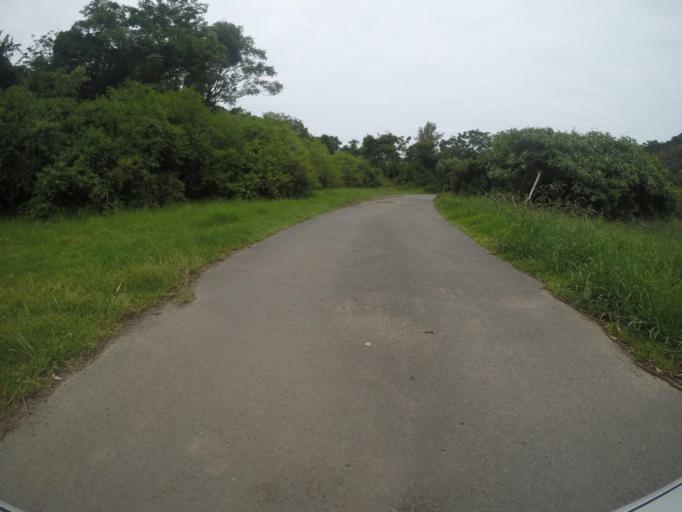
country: ZA
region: Eastern Cape
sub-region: Buffalo City Metropolitan Municipality
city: East London
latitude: -32.9757
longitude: 27.9282
